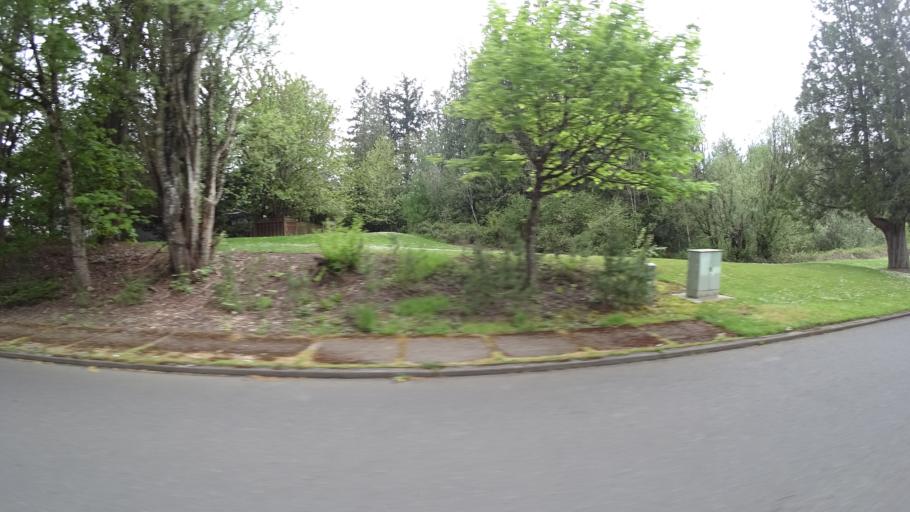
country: US
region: Oregon
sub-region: Washington County
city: Rockcreek
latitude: 45.5482
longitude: -122.8814
